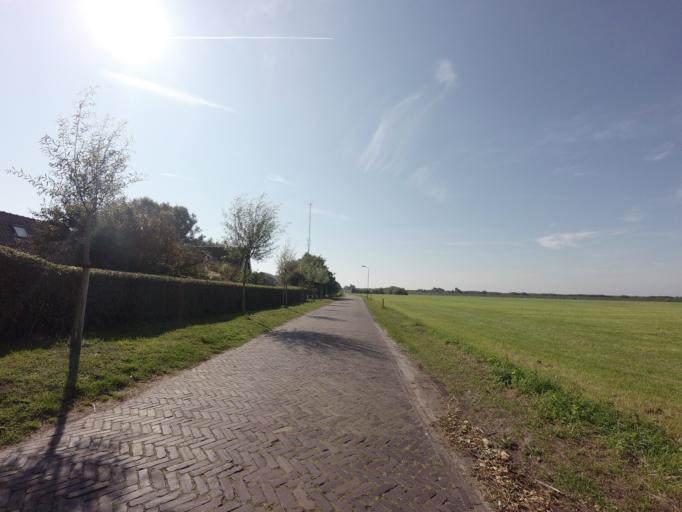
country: NL
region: Friesland
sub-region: Gemeente Schiermonnikoog
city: Schiermonnikoog
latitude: 53.4778
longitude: 6.1544
